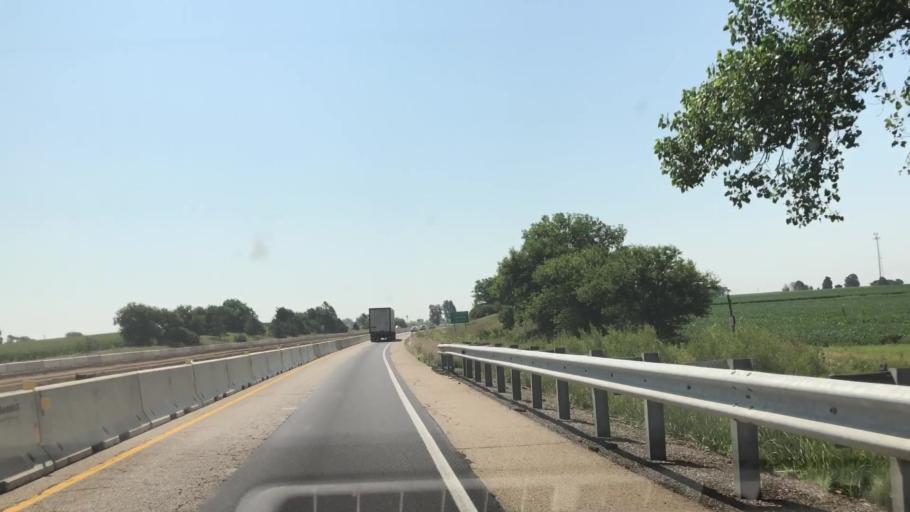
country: US
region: Illinois
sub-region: McLean County
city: Danvers
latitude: 40.5908
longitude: -89.1511
